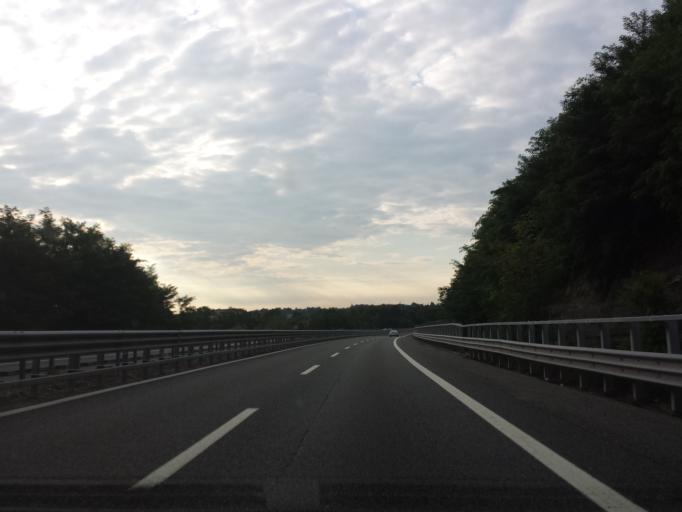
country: IT
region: Lombardy
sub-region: Provincia di Varese
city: Cavaria Con Premezzo
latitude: 45.6850
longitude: 8.7884
